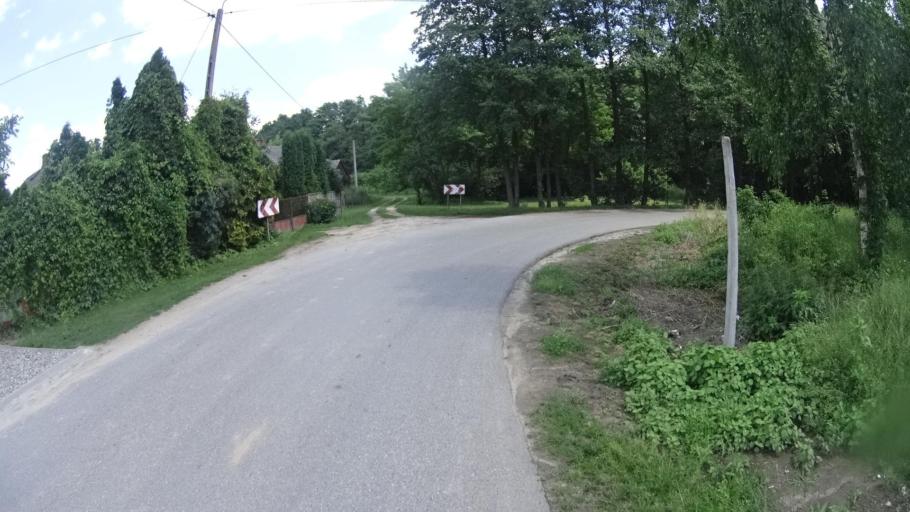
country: PL
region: Masovian Voivodeship
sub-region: Powiat grojecki
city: Goszczyn
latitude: 51.6970
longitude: 20.8740
